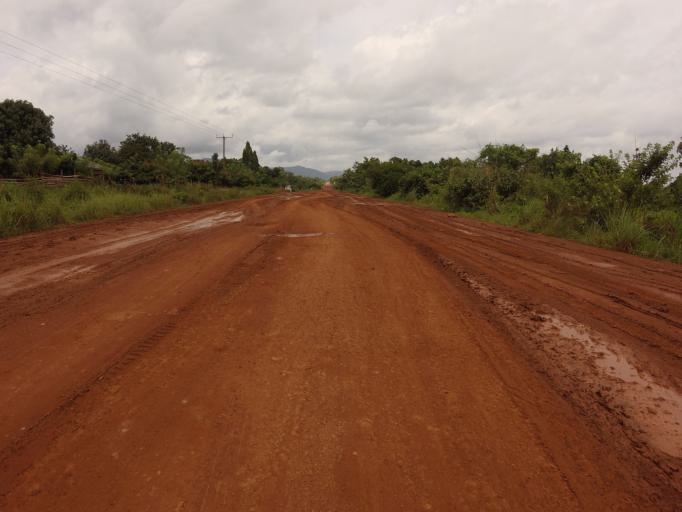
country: GH
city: Kpandae
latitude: 8.2808
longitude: 0.5050
